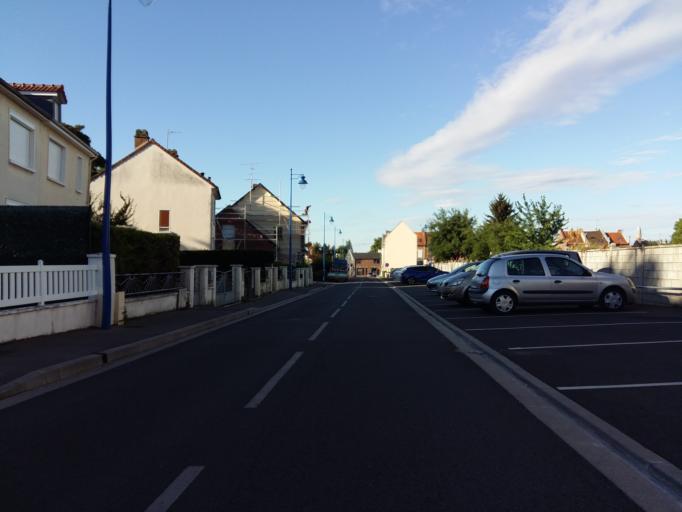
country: FR
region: Picardie
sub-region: Departement de la Somme
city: Rivery
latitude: 49.9034
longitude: 2.3256
